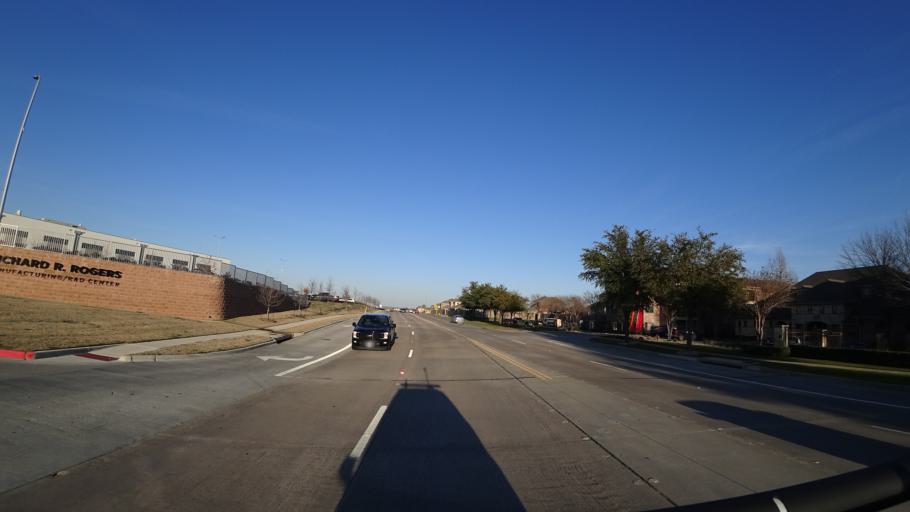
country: US
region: Texas
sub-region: Dallas County
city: Coppell
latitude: 32.9960
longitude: -96.9911
